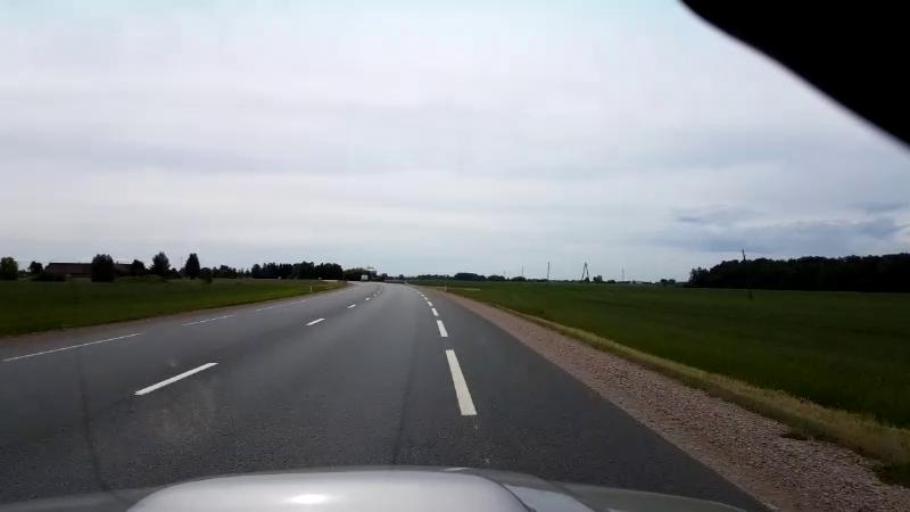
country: LV
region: Bauskas Rajons
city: Bauska
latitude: 56.4442
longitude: 24.1665
